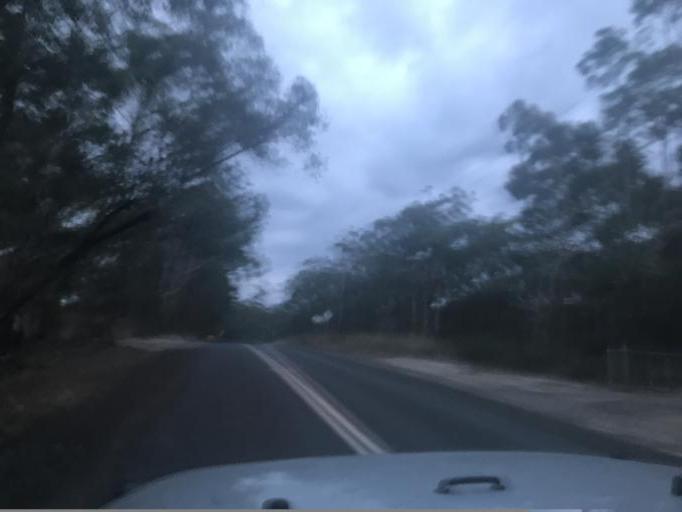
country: AU
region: New South Wales
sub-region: Hawkesbury
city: Pitt Town
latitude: -33.5042
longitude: 150.8673
